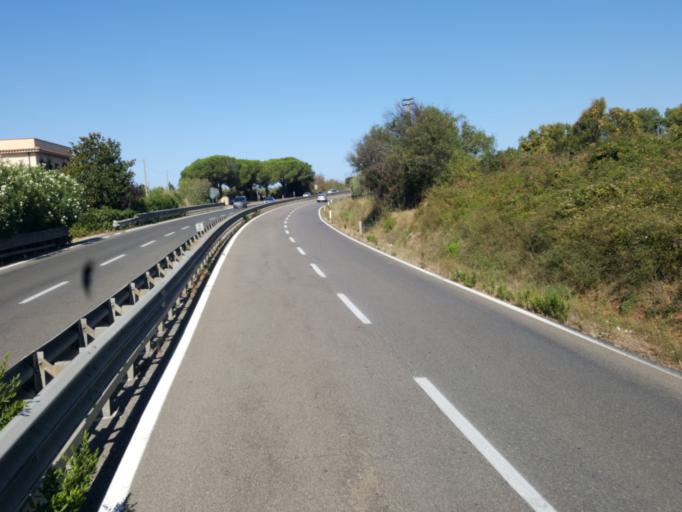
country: IT
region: Tuscany
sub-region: Provincia di Grosseto
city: Orbetello Scalo
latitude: 42.4407
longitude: 11.2656
